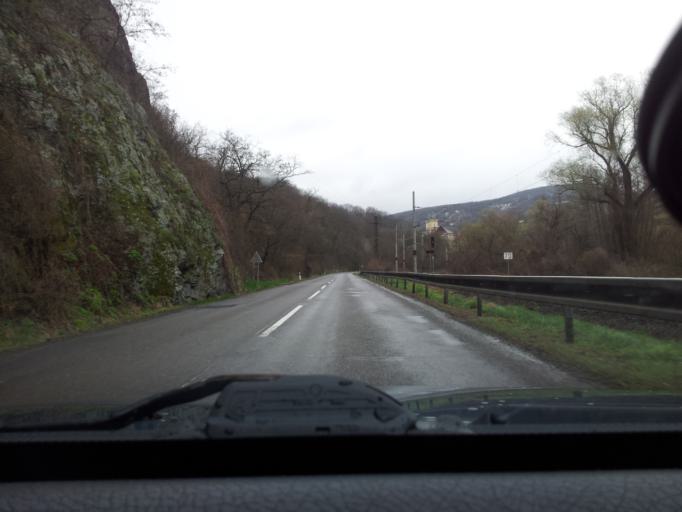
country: SK
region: Nitriansky
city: Tlmace
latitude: 48.3389
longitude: 18.5581
